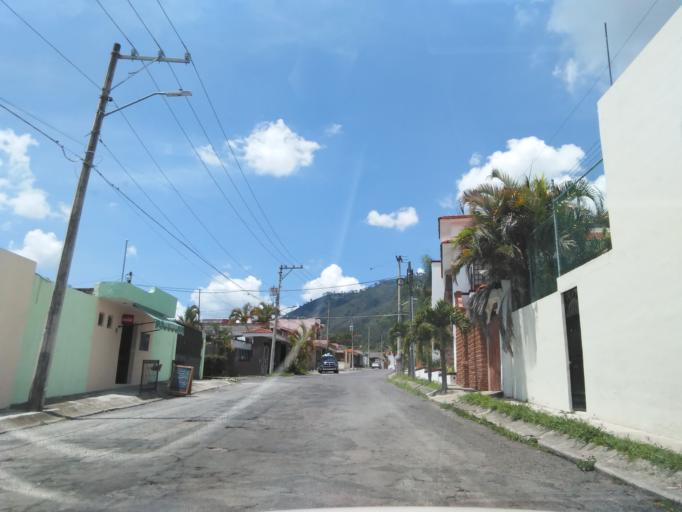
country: MX
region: Nayarit
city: Tepic
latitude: 21.5166
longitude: -104.9201
